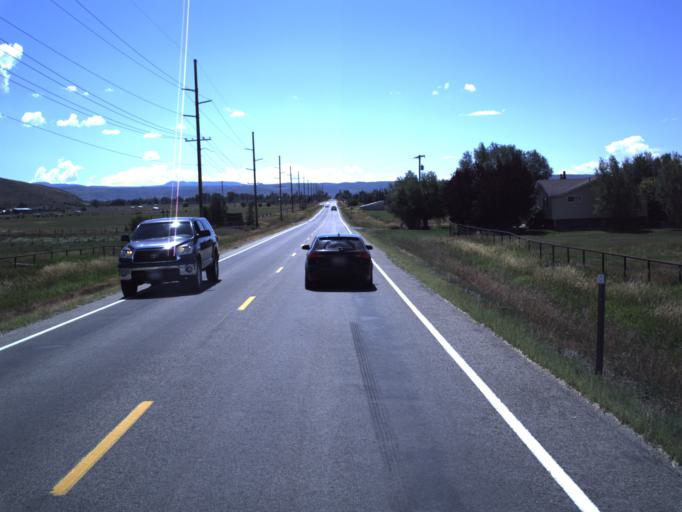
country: US
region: Utah
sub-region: Summit County
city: Kamas
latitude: 40.6673
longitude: -111.2808
